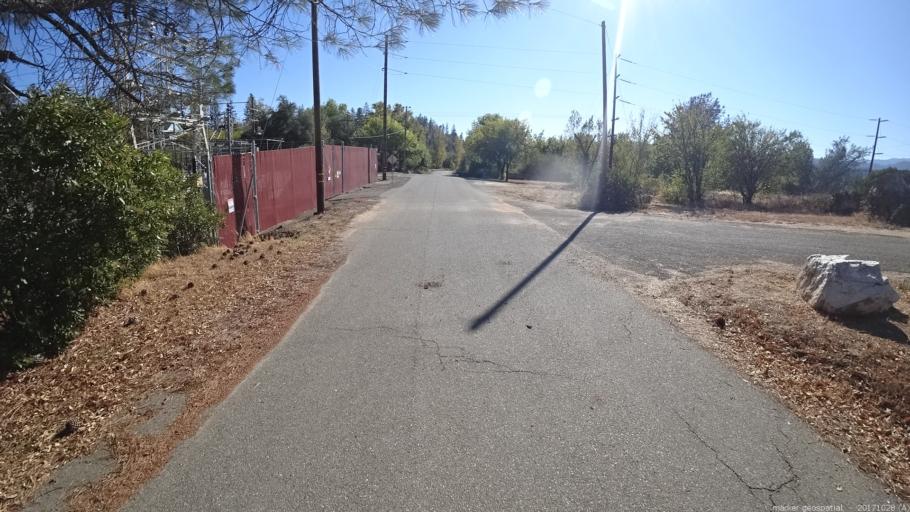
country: US
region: California
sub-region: Shasta County
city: Shasta
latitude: 40.6241
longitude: -122.4624
